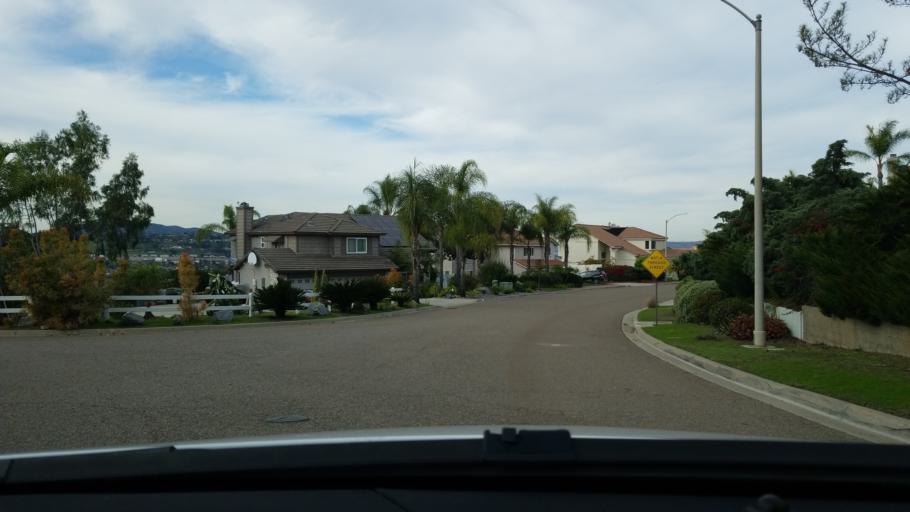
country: US
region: California
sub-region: San Diego County
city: Casa de Oro-Mount Helix
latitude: 32.7745
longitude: -116.9565
